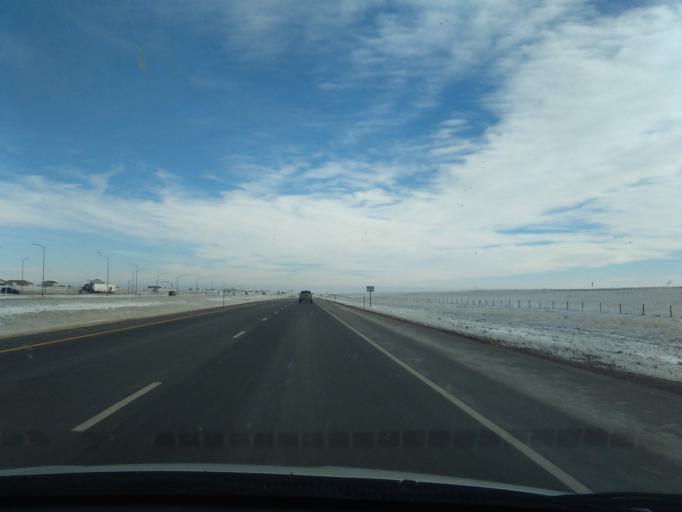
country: US
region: Wyoming
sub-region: Laramie County
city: Fox Farm-College
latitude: 41.1582
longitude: -104.6346
